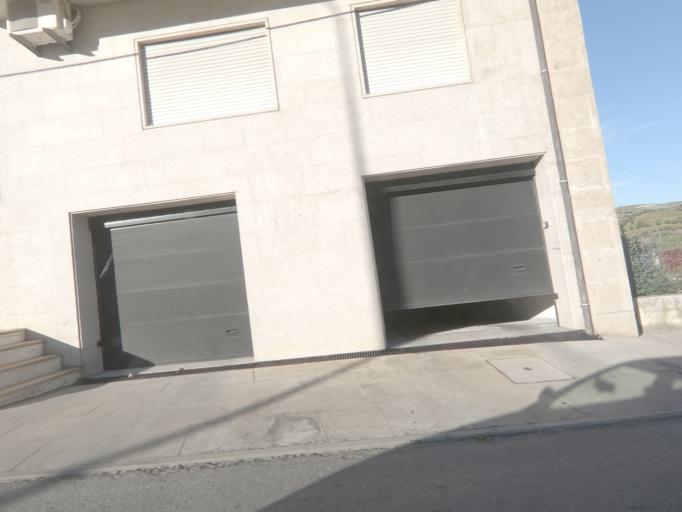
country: PT
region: Vila Real
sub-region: Peso da Regua
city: Godim
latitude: 41.1684
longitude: -7.8000
